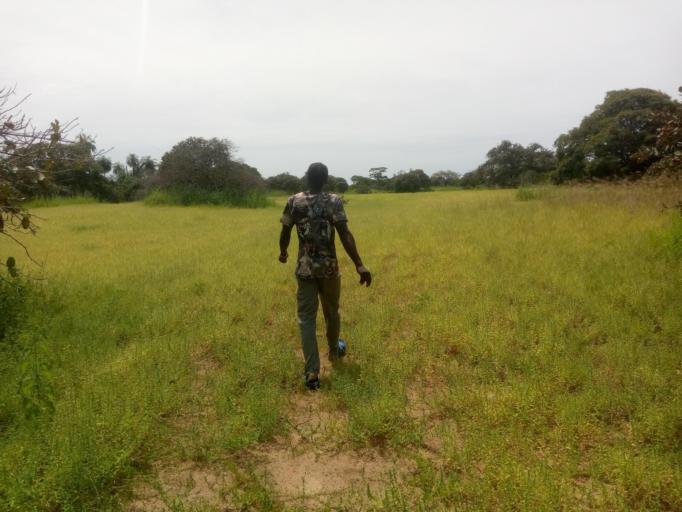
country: GM
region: Western
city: Gunjur
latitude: 13.0544
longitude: -16.7349
